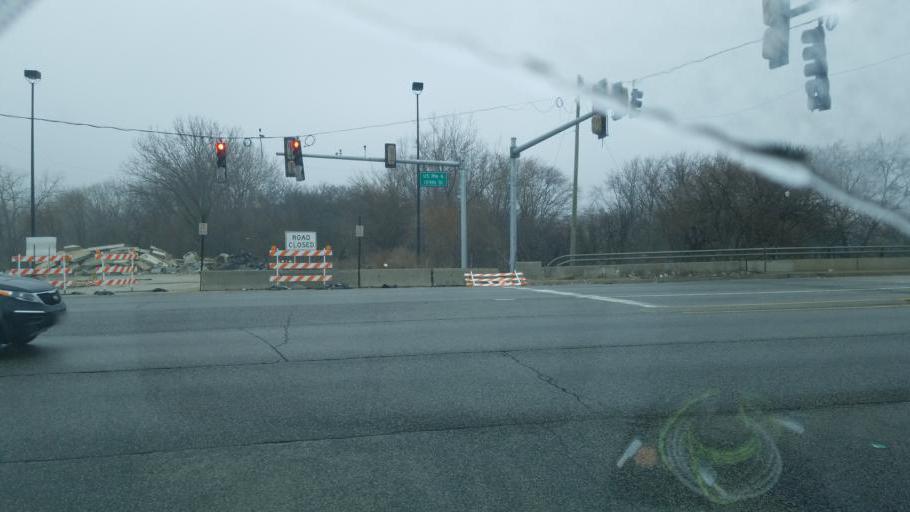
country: US
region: Illinois
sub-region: Cook County
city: South Holland
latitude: 41.6008
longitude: -87.5782
